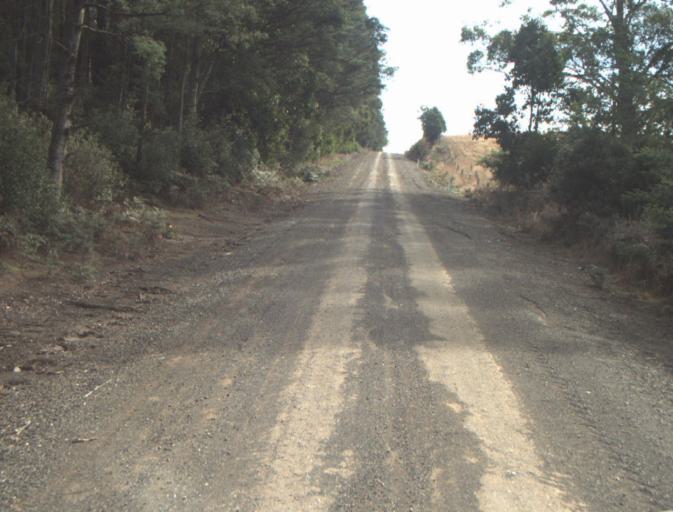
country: AU
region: Tasmania
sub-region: Launceston
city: Mayfield
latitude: -41.1965
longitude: 147.2111
